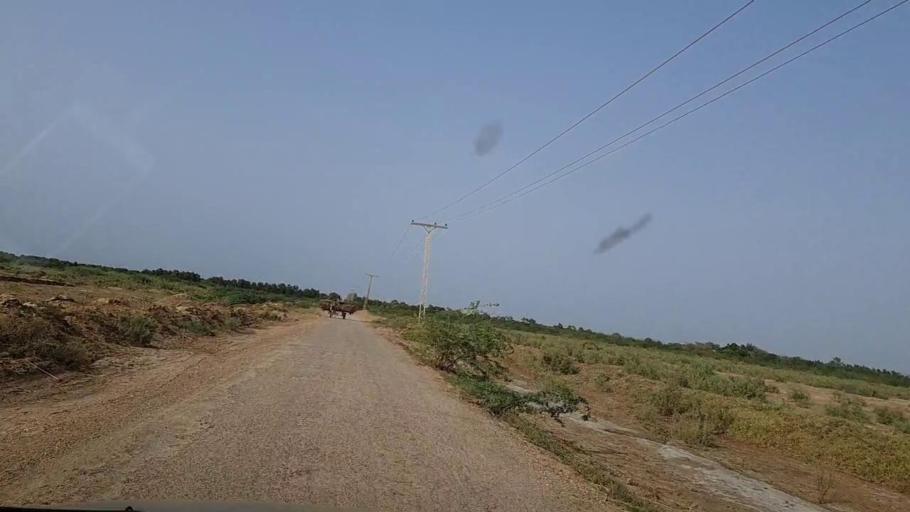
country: PK
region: Sindh
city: Kotri
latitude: 25.2209
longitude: 68.2465
